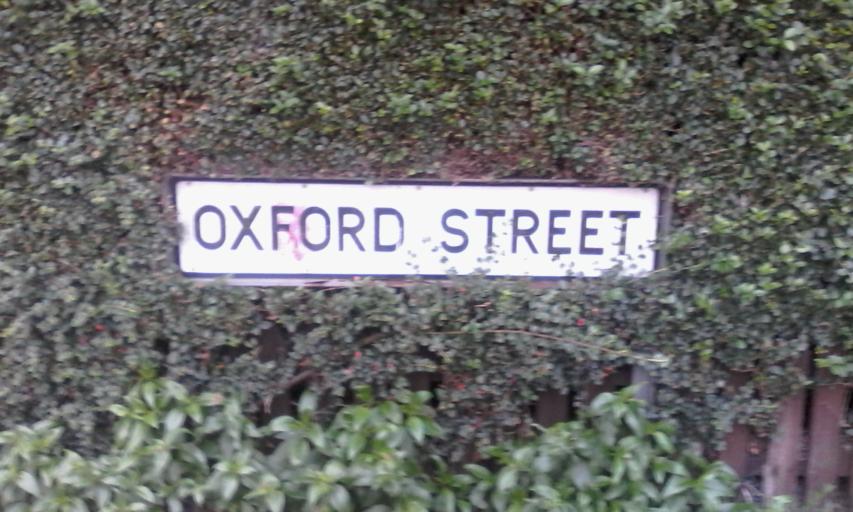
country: GB
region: England
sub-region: Nottinghamshire
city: Radcliffe on Trent
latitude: 52.9714
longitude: -1.0867
